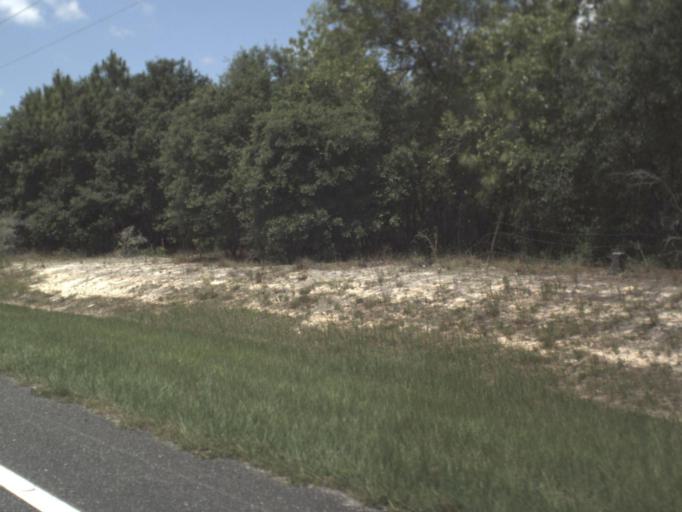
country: US
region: Florida
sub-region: Levy County
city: Williston Highlands
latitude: 29.2378
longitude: -82.5585
